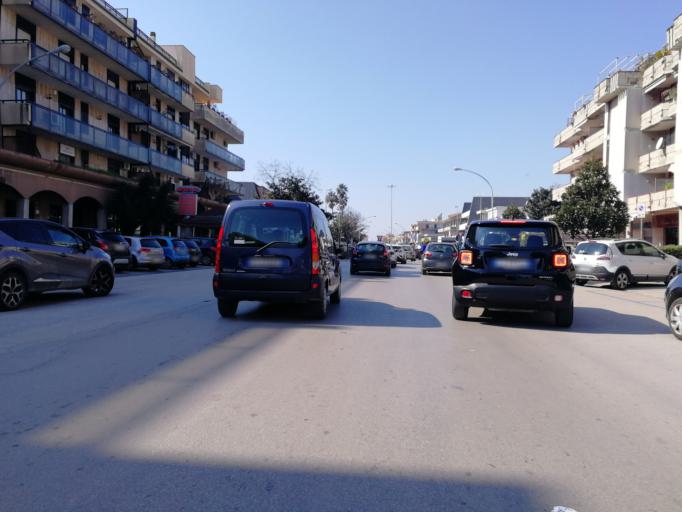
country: IT
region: Campania
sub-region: Provincia di Caserta
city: Santa Maria Capua Vetere
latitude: 41.0901
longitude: 14.2547
